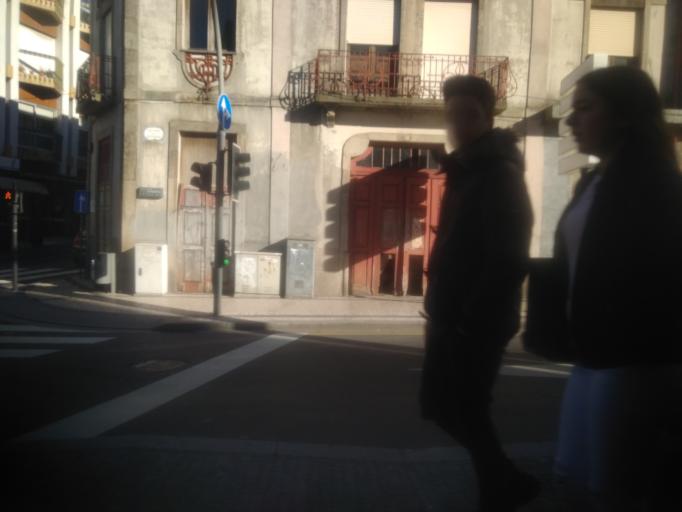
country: PT
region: Porto
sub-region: Vila Nova de Gaia
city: Vila Nova de Gaia
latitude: 41.1342
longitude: -8.6075
